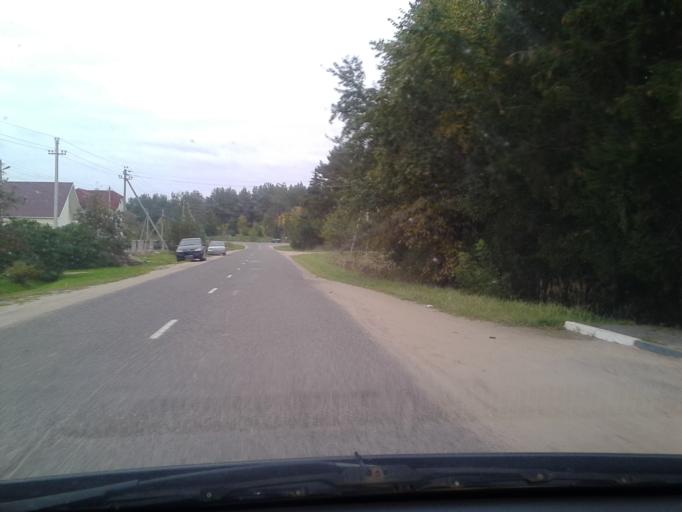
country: BY
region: Vitebsk
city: Pastavy
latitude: 55.0937
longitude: 26.8408
